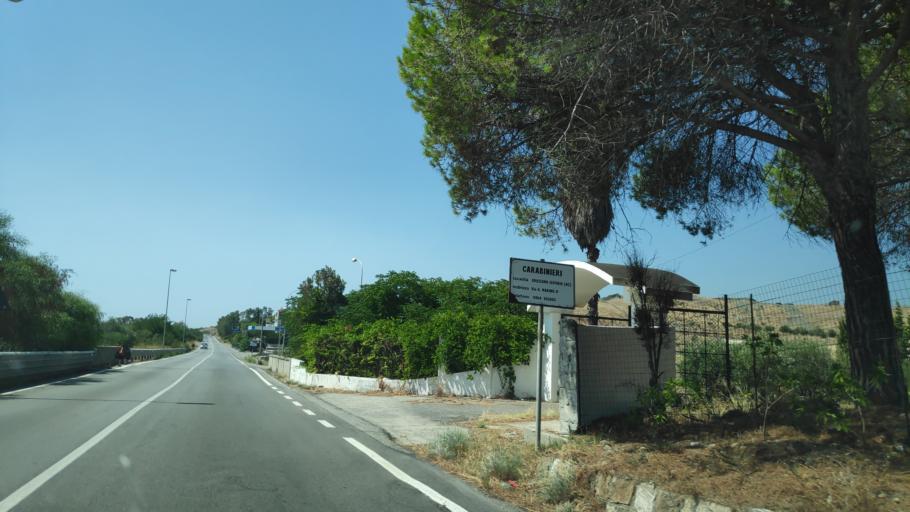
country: IT
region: Calabria
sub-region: Provincia di Reggio Calabria
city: Africo Nuovo
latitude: 38.0108
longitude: 16.1306
